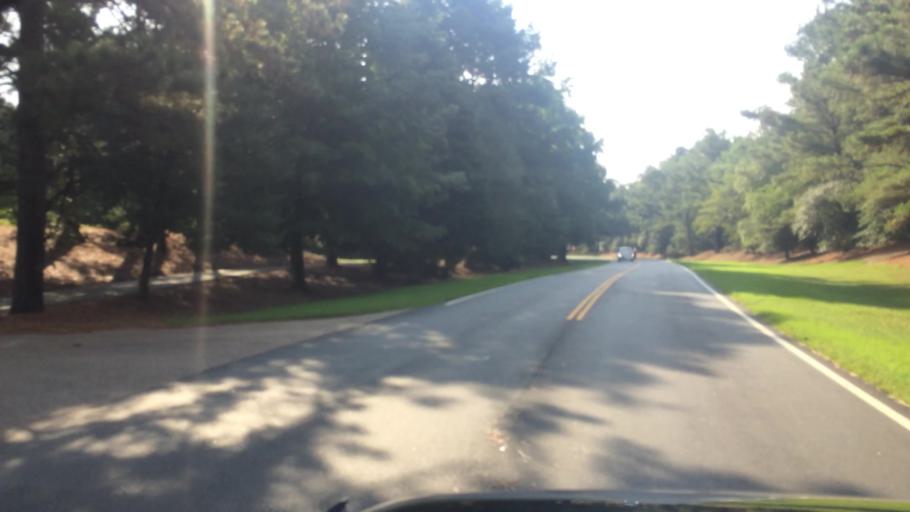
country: US
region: Virginia
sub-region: City of Williamsburg
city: Williamsburg
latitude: 37.2323
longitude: -76.6557
